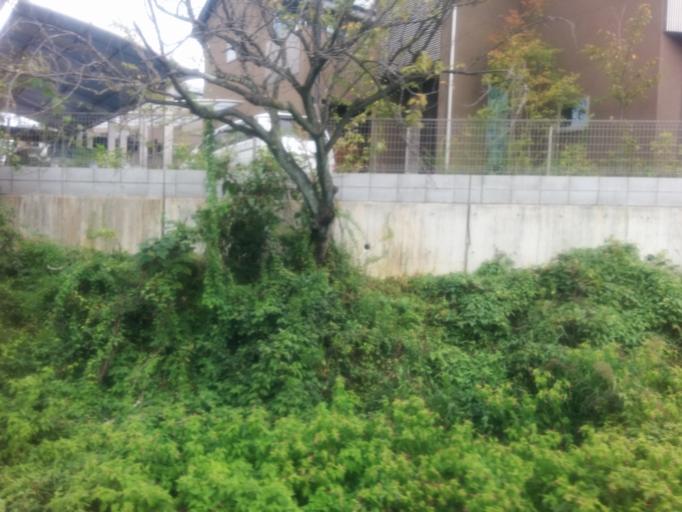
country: JP
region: Kyoto
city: Uji
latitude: 34.9329
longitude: 135.7711
